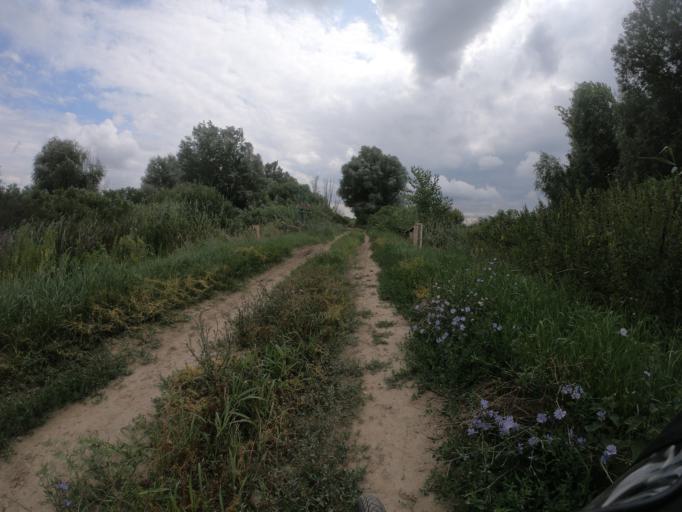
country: HU
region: Jasz-Nagykun-Szolnok
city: Tiszafured
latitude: 47.7059
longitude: 20.7768
